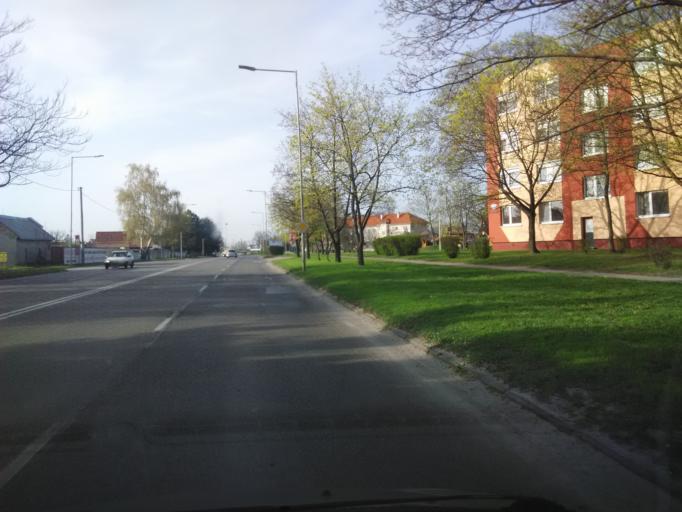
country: SK
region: Nitriansky
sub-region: Okres Nove Zamky
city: Nove Zamky
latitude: 47.9958
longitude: 18.1666
